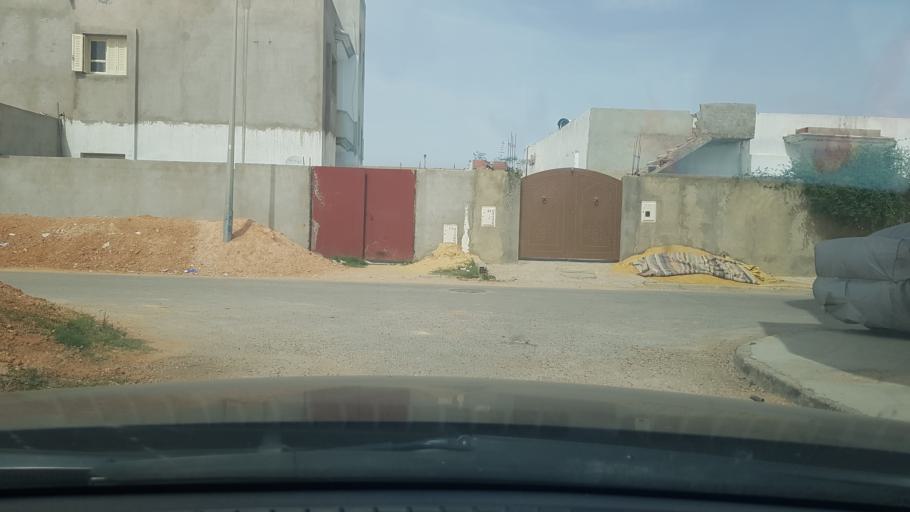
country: TN
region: Safaqis
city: Al Qarmadah
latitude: 34.8257
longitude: 10.7507
